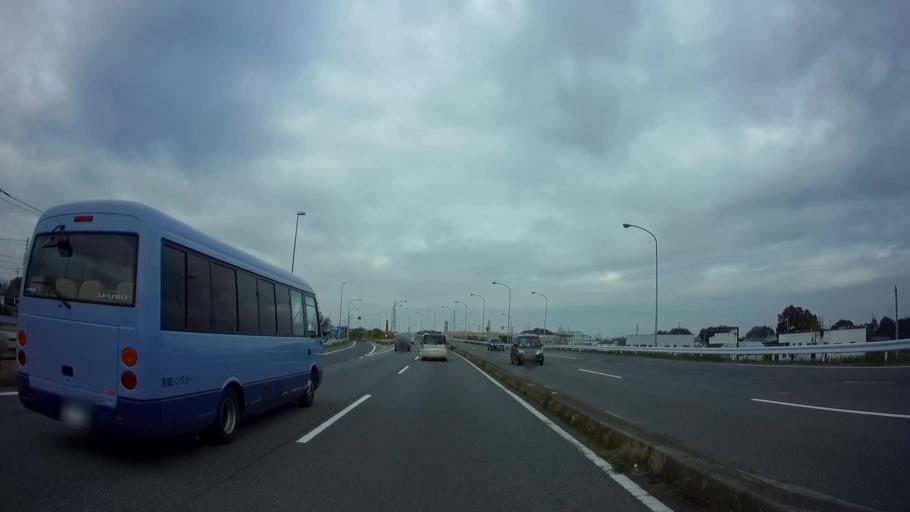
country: JP
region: Saitama
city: Kumagaya
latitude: 36.1718
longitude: 139.3741
